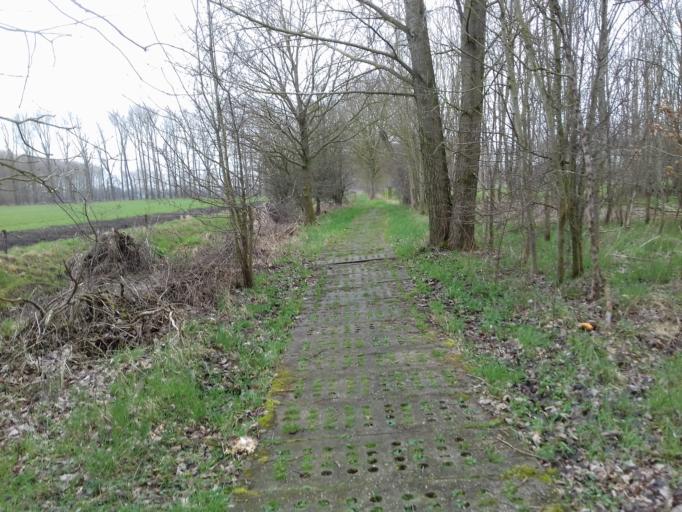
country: NL
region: Gelderland
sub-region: Gemeente Culemborg
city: Culemborg
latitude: 51.9064
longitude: 5.2275
